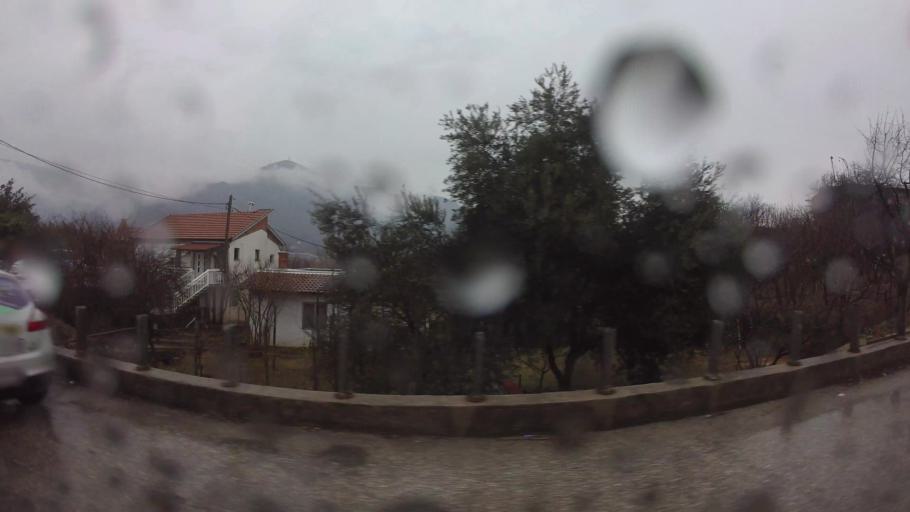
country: BA
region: Federation of Bosnia and Herzegovina
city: Cim
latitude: 43.3463
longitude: 17.7907
